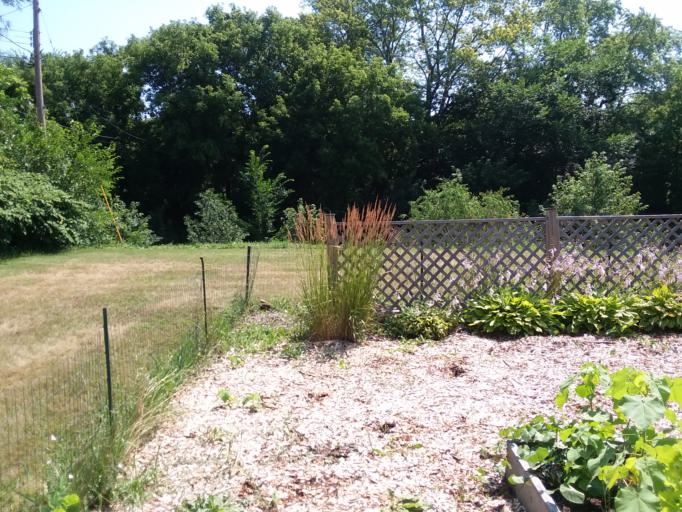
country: US
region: Wisconsin
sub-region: Milwaukee County
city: Brown Deer
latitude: 43.1094
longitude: -87.9910
